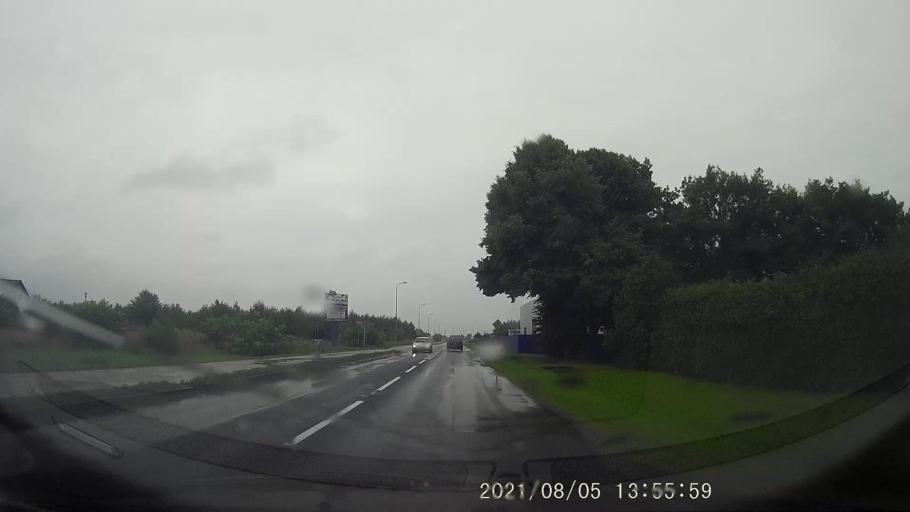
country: PL
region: Opole Voivodeship
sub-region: Powiat krapkowicki
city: Krapkowice
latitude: 50.4659
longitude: 17.9491
